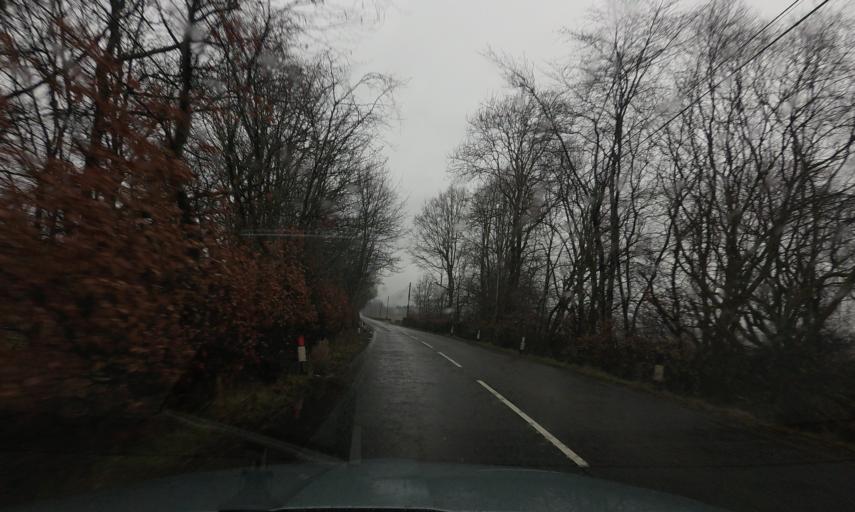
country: GB
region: Scotland
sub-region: Stirling
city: Balfron
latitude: 56.1471
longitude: -4.3599
